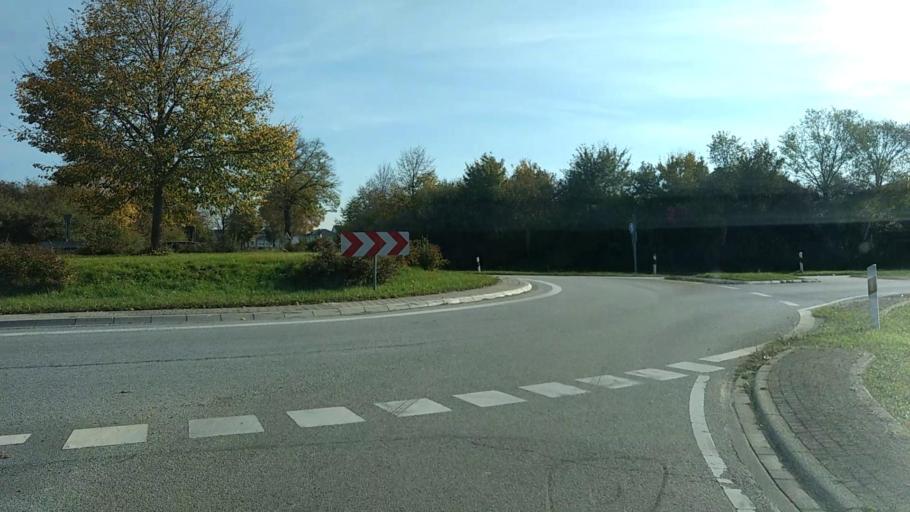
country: DE
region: North Rhine-Westphalia
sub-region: Regierungsbezirk Koln
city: Bergheim
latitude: 50.9106
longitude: 6.6592
